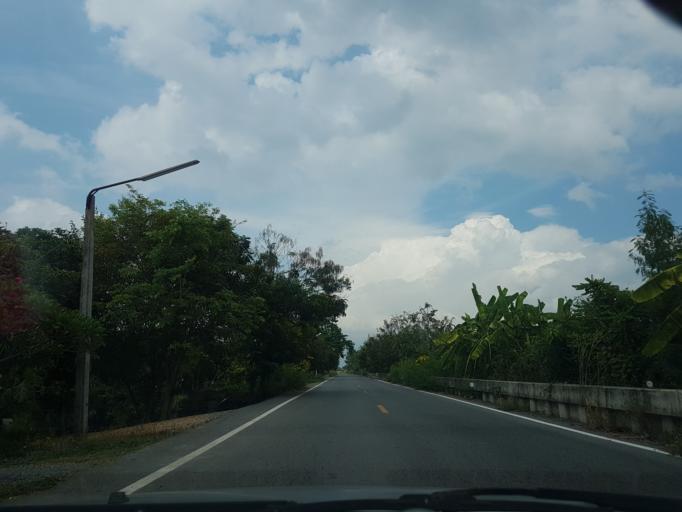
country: TH
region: Sara Buri
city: Nong Khae
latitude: 14.2563
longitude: 100.8913
